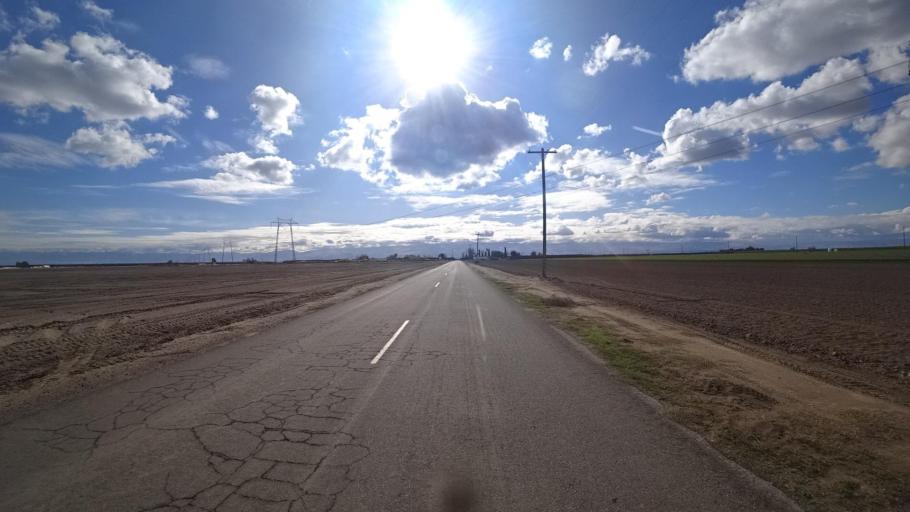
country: US
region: California
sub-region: Kern County
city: Greenfield
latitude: 35.2226
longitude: -119.0923
